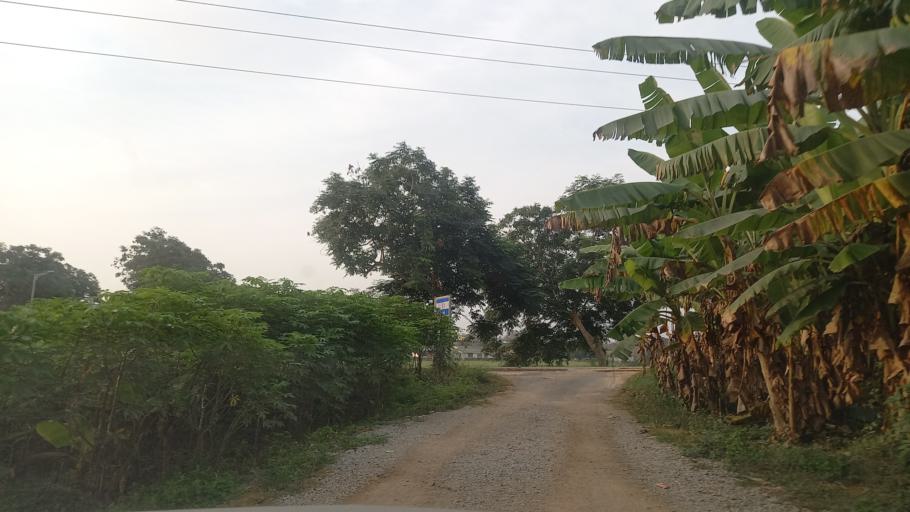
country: GH
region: Western
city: Shama Junction
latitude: 4.9847
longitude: -1.6581
